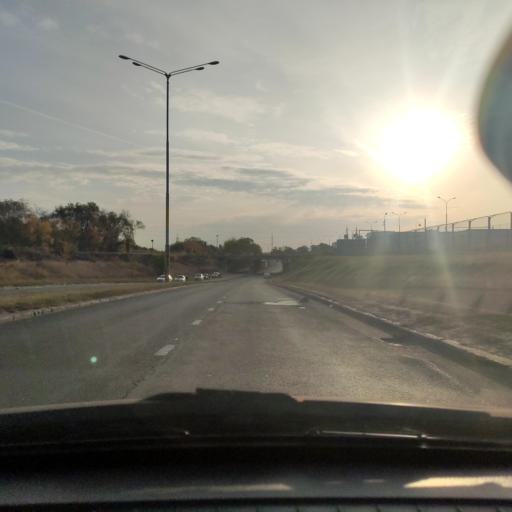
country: RU
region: Samara
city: Tol'yatti
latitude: 53.5674
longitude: 49.2818
